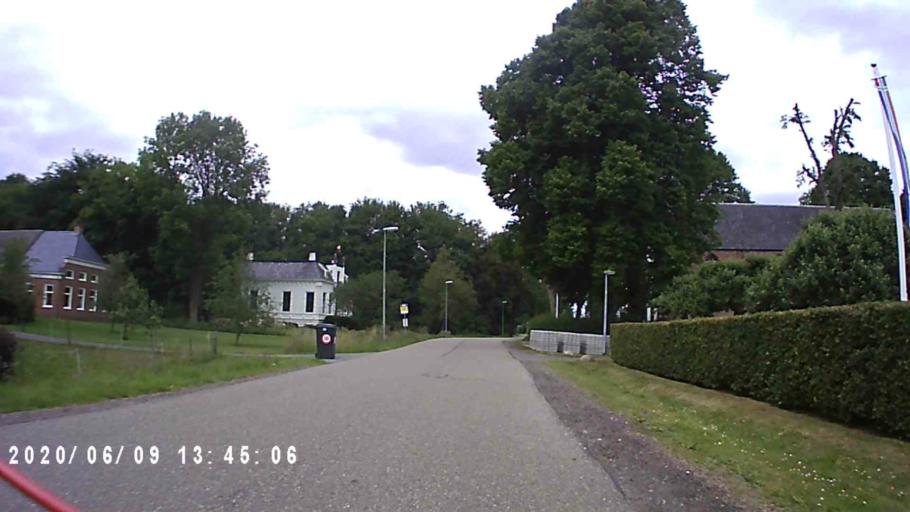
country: NL
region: Groningen
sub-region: Gemeente Groningen
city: Oosterpark
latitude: 53.2219
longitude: 6.6367
